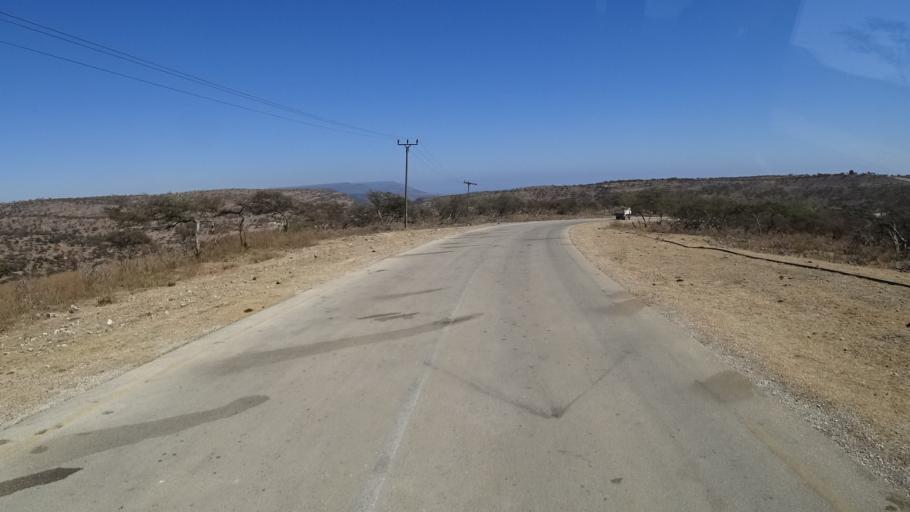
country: YE
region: Al Mahrah
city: Hawf
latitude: 16.7906
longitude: 53.3256
